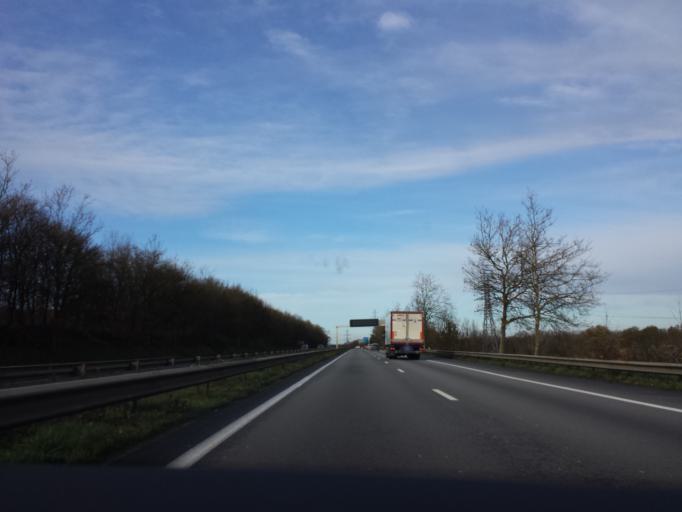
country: FR
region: Ile-de-France
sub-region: Departement des Yvelines
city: Saint-Cyr-l'Ecole
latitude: 48.7902
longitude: 2.0584
